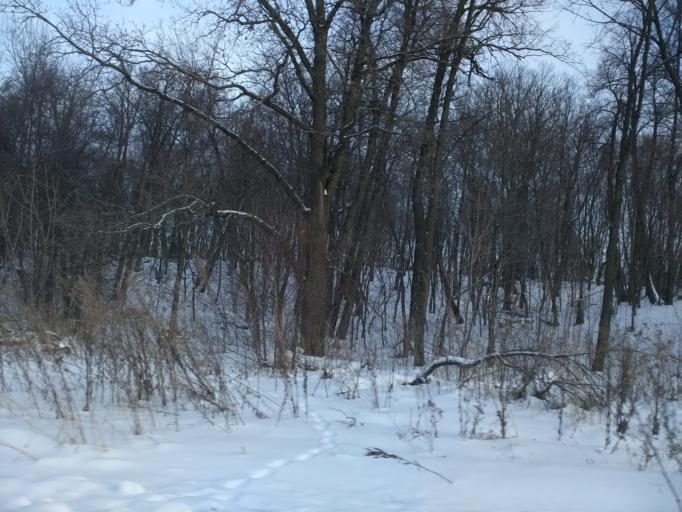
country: RU
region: Bashkortostan
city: Iglino
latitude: 54.7735
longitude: 56.5460
